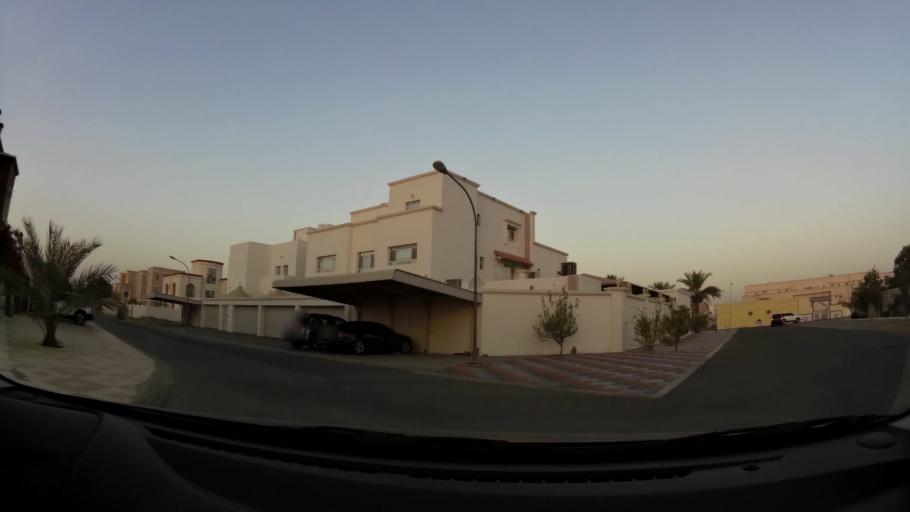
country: OM
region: Muhafazat Masqat
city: As Sib al Jadidah
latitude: 23.6455
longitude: 58.2150
